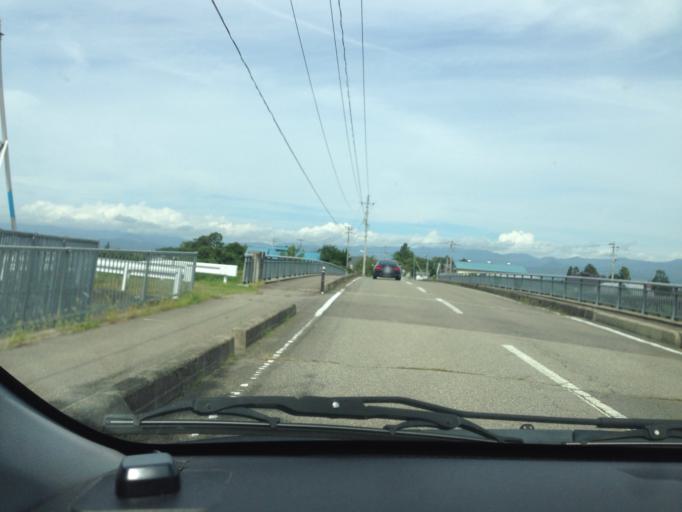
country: JP
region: Fukushima
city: Kitakata
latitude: 37.5757
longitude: 139.8881
